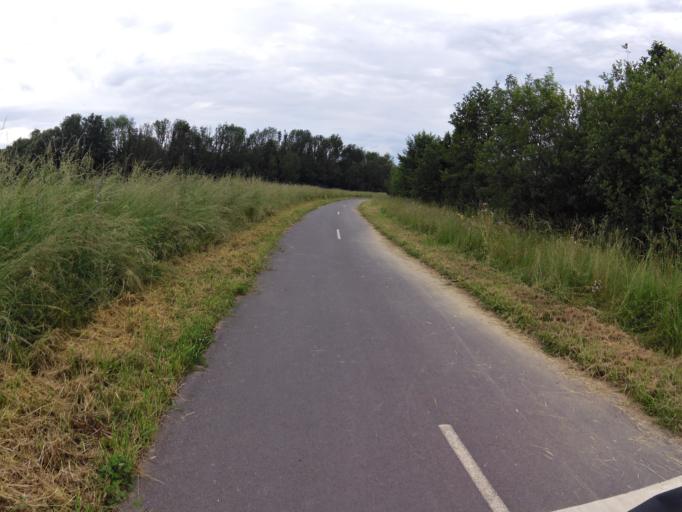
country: FR
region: Champagne-Ardenne
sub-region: Departement des Ardennes
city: Donchery
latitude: 49.7052
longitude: 4.8978
